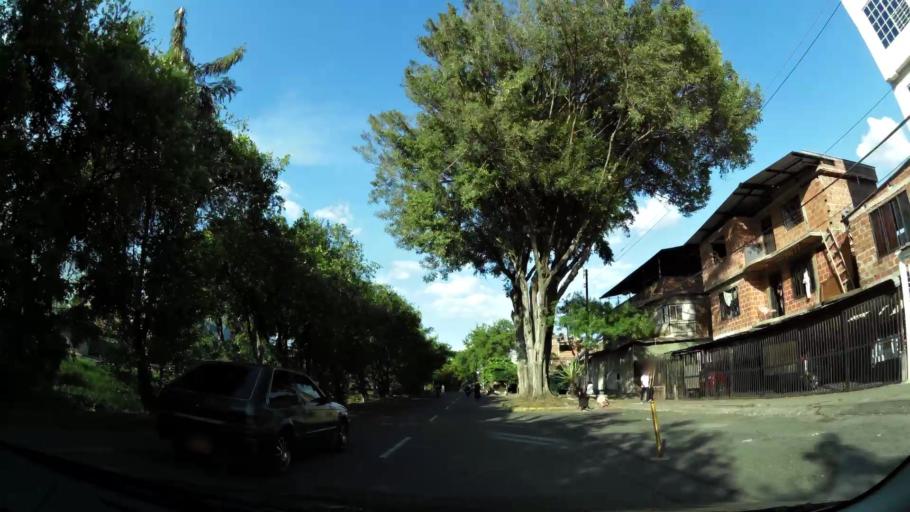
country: CO
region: Valle del Cauca
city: Cali
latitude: 3.4055
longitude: -76.5069
